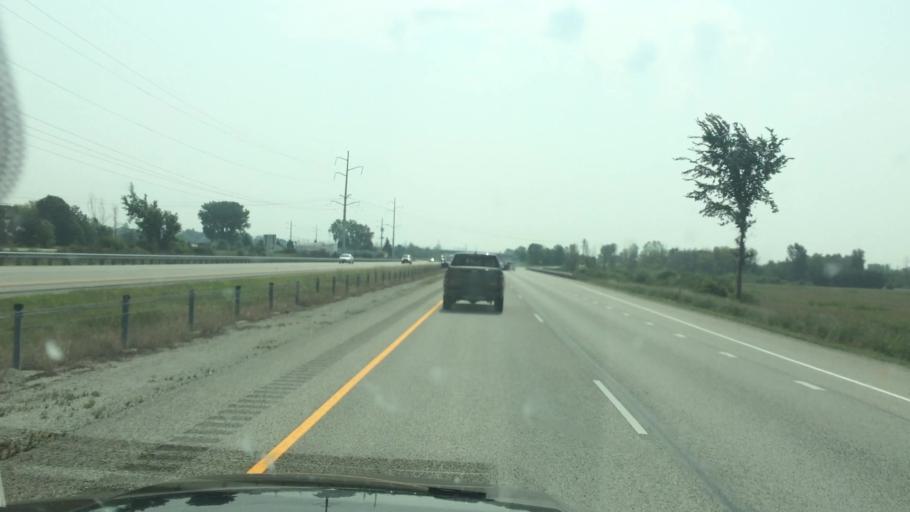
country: US
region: Wisconsin
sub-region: Fond du Lac County
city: North Fond du Lac
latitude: 43.8100
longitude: -88.5060
